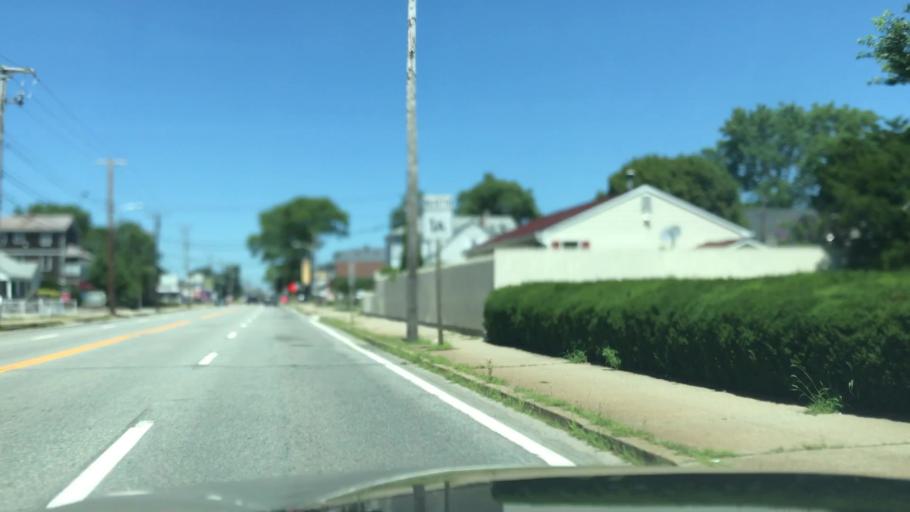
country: US
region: Rhode Island
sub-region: Providence County
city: Pawtucket
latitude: 41.8706
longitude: -71.3543
